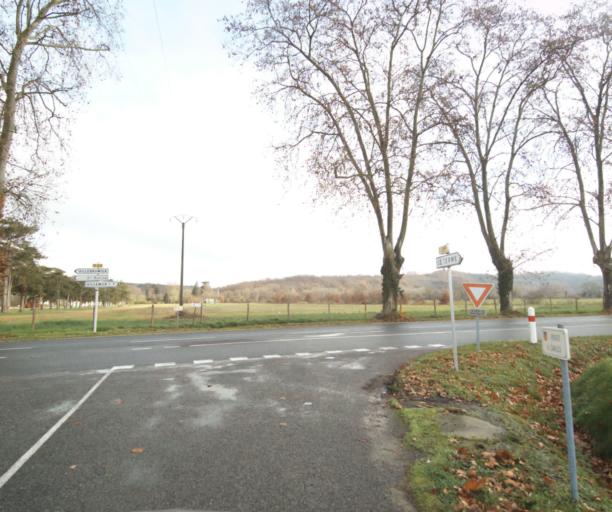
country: FR
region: Midi-Pyrenees
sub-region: Departement de la Haute-Garonne
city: Villemur-sur-Tarn
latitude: 43.8834
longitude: 1.4813
